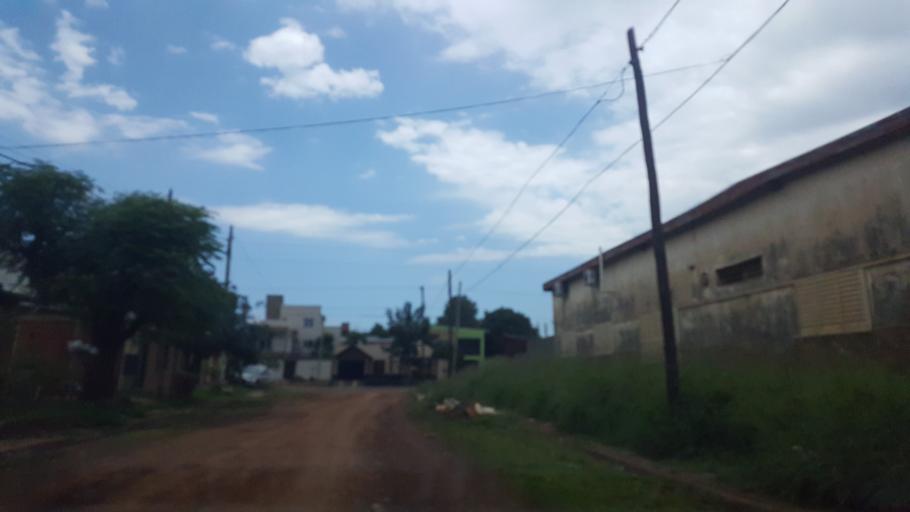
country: AR
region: Misiones
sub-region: Departamento de Capital
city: Posadas
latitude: -27.3752
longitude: -55.9158
